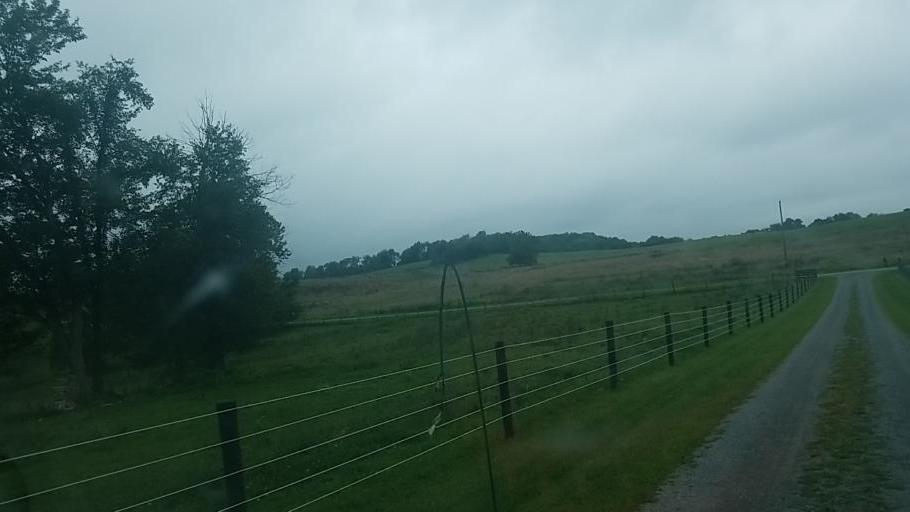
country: US
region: Ohio
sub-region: Knox County
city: Danville
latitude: 40.4914
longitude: -82.1542
